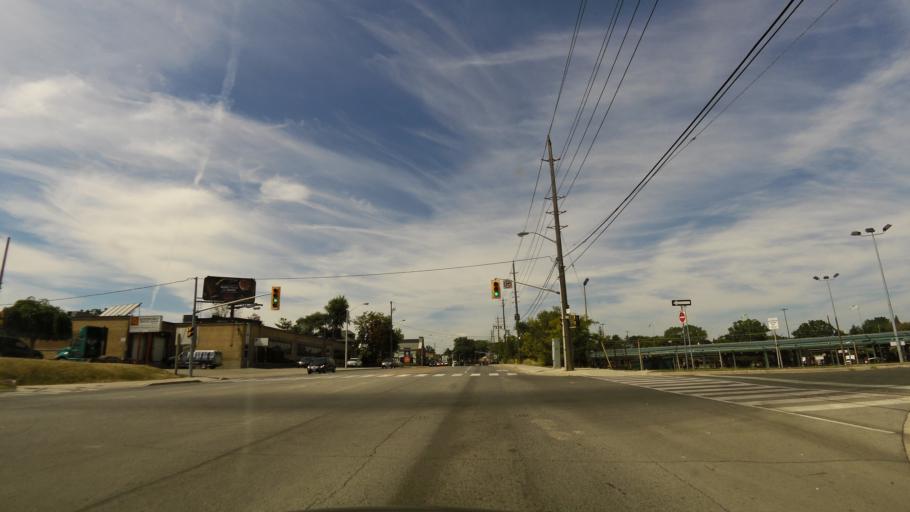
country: CA
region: Ontario
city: Etobicoke
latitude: 43.6270
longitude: -79.4875
